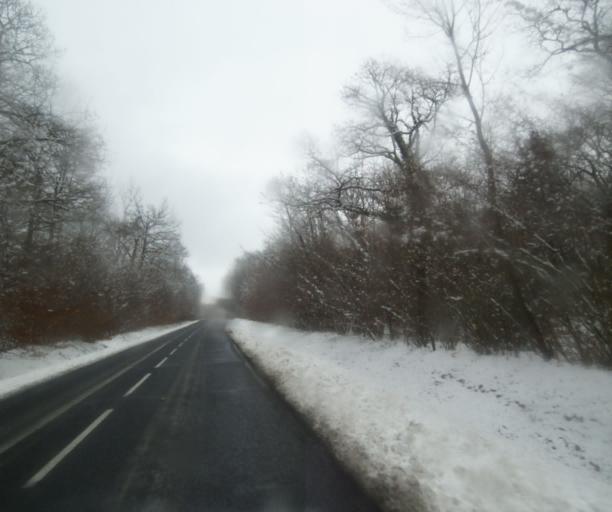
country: FR
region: Champagne-Ardenne
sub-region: Departement de la Haute-Marne
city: Laneuville-a-Remy
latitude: 48.4588
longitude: 4.8876
